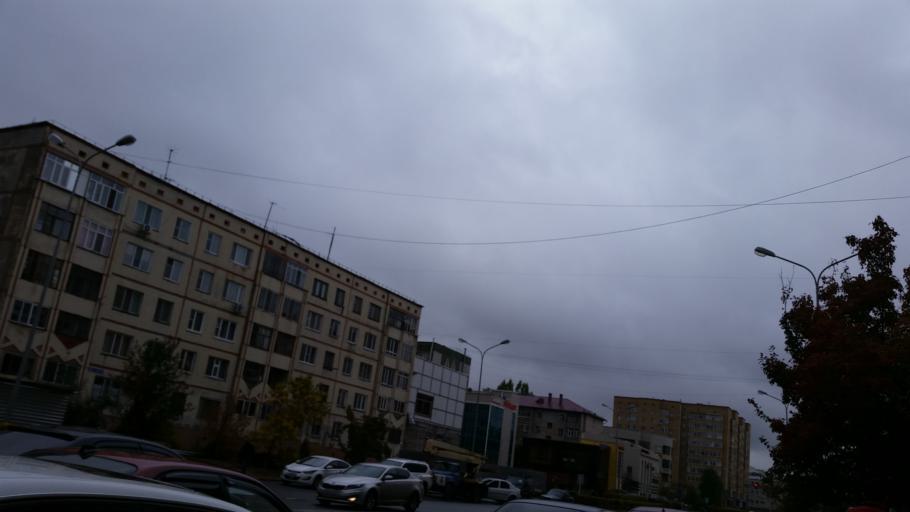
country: KZ
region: Astana Qalasy
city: Astana
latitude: 51.1547
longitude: 71.5026
